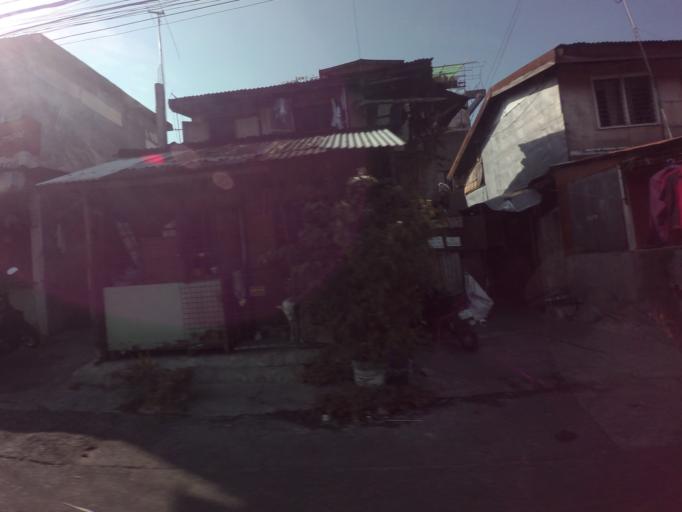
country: PH
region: Calabarzon
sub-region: Province of Rizal
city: Taguig
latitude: 14.4972
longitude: 121.0508
